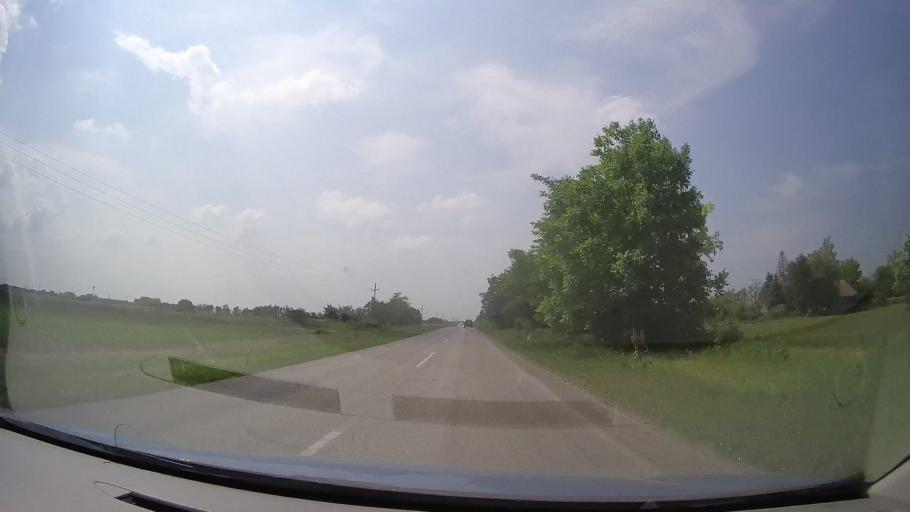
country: RS
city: Crepaja
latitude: 44.9991
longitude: 20.6401
